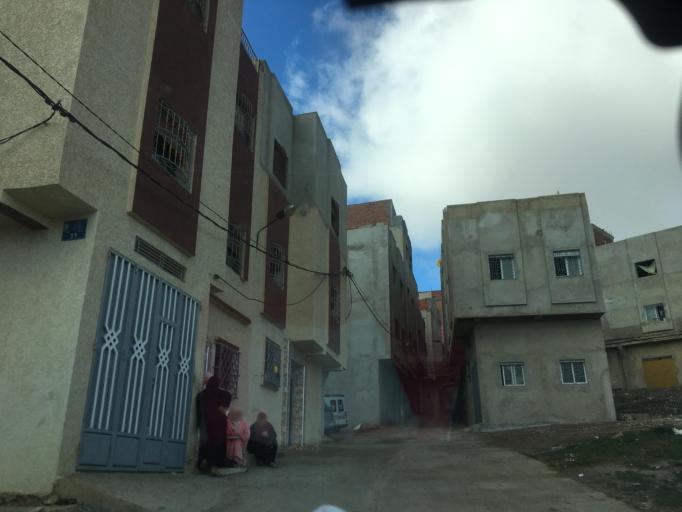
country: MA
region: Tanger-Tetouan
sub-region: Tanger-Assilah
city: Tangier
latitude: 35.7149
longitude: -5.8086
